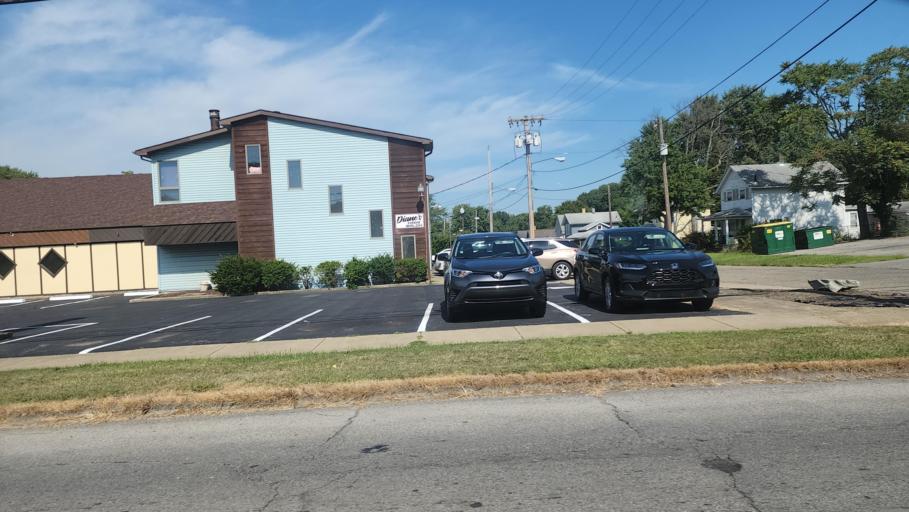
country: US
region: Ohio
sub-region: Trumbull County
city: Niles
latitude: 41.1868
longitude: -80.7560
